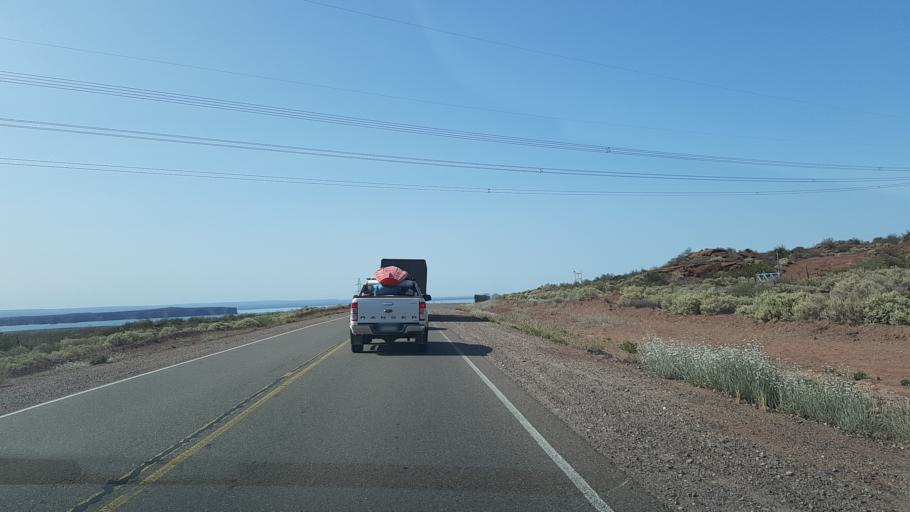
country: AR
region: Neuquen
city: Plaza Huincul
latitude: -39.2701
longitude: -68.8548
